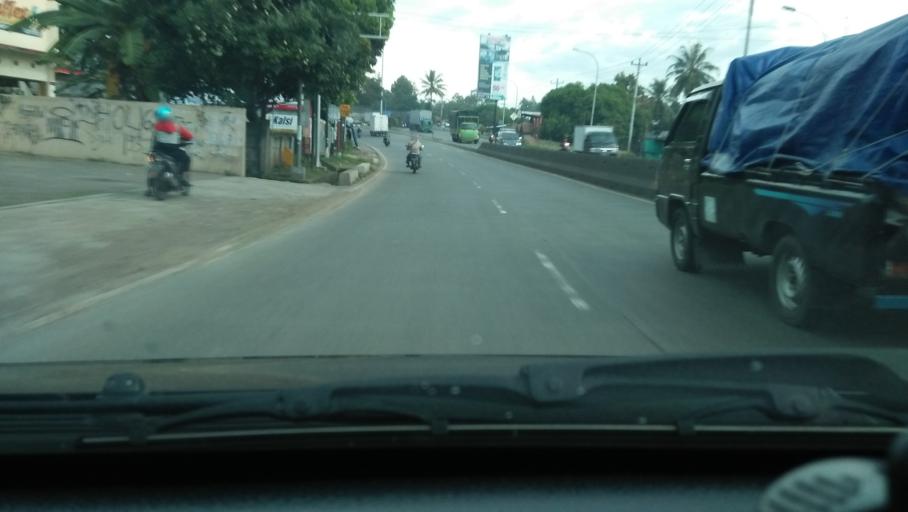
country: ID
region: Central Java
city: Ungaran
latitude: -7.1023
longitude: 110.4091
